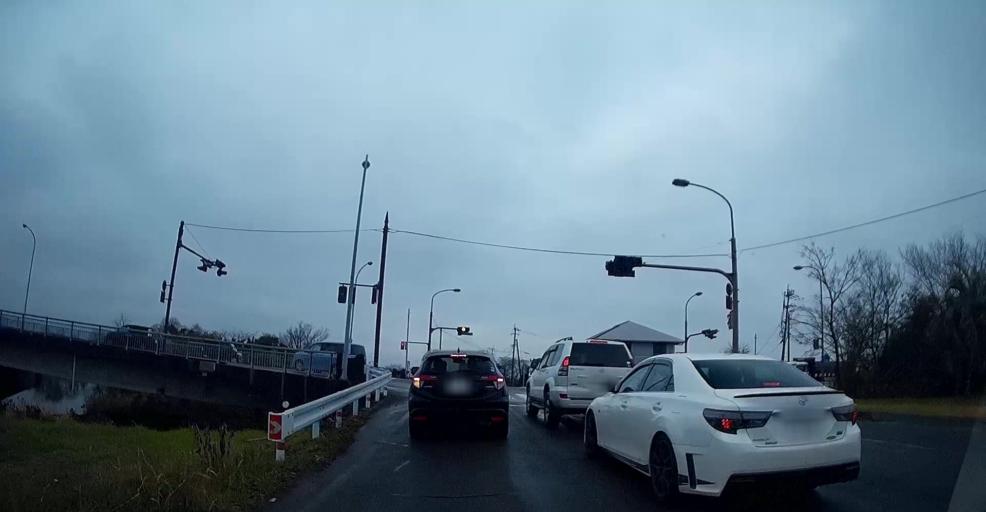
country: JP
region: Kumamoto
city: Kumamoto
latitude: 32.7531
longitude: 130.7381
